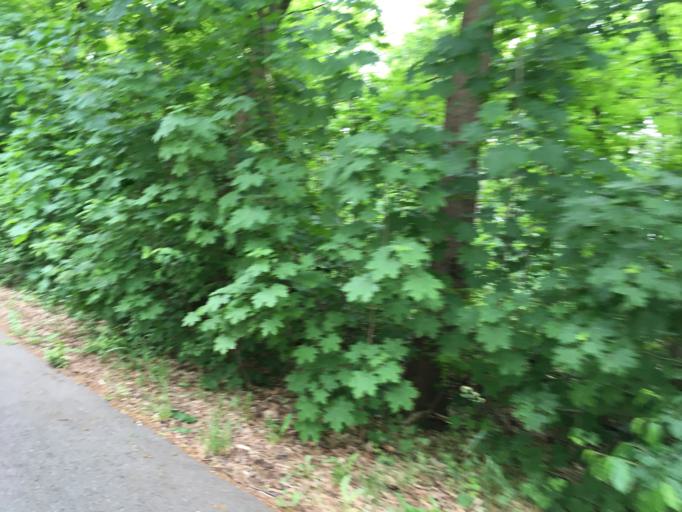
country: DE
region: Brandenburg
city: Bernau bei Berlin
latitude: 52.6887
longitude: 13.5651
